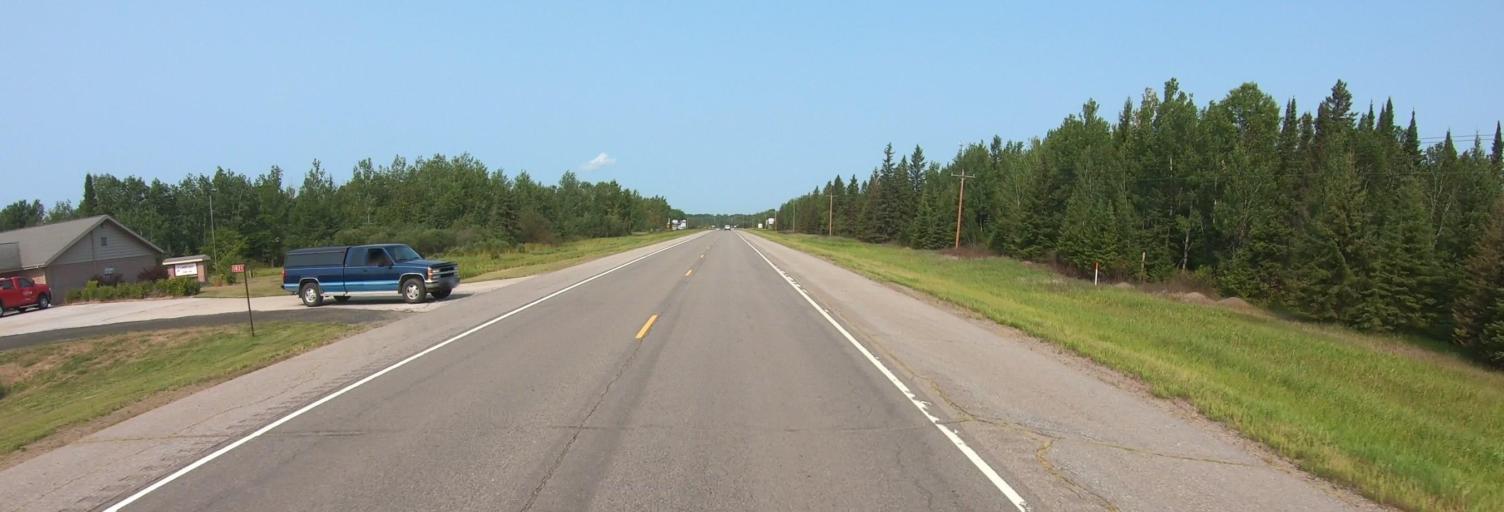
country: US
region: Minnesota
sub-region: Saint Louis County
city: Mountain Iron
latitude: 47.8567
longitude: -92.7050
